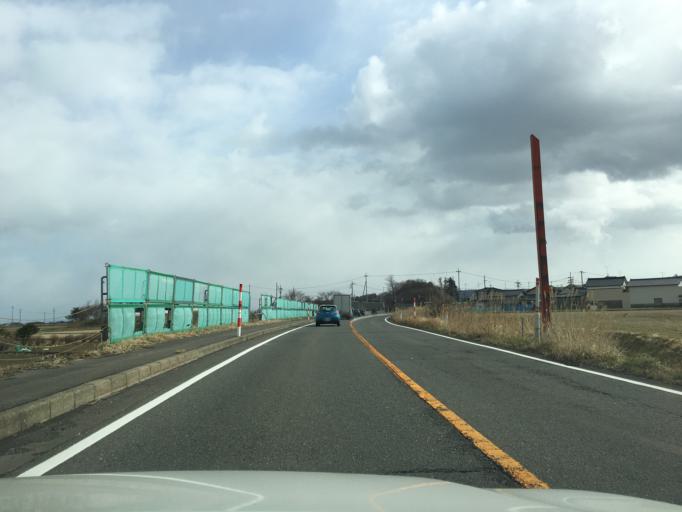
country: JP
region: Yamagata
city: Yuza
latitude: 39.2768
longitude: 139.9267
